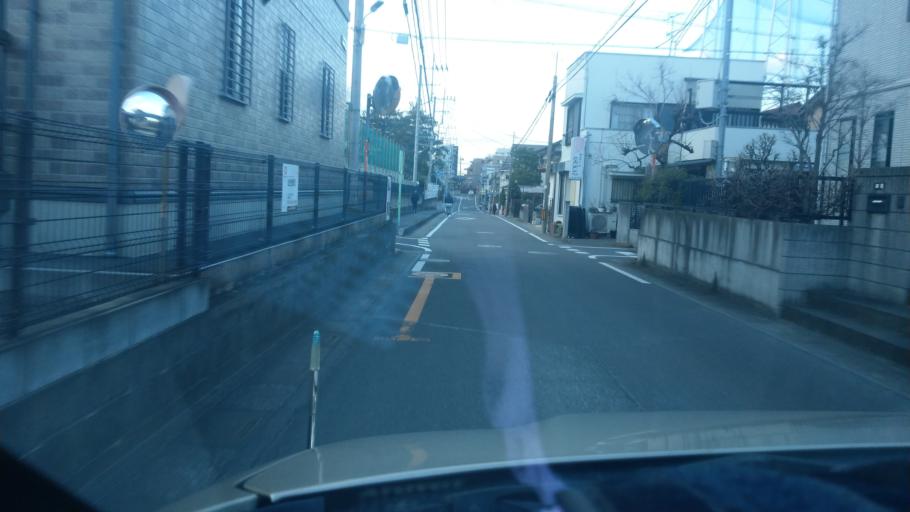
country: JP
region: Saitama
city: Yono
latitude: 35.8951
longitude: 139.6005
